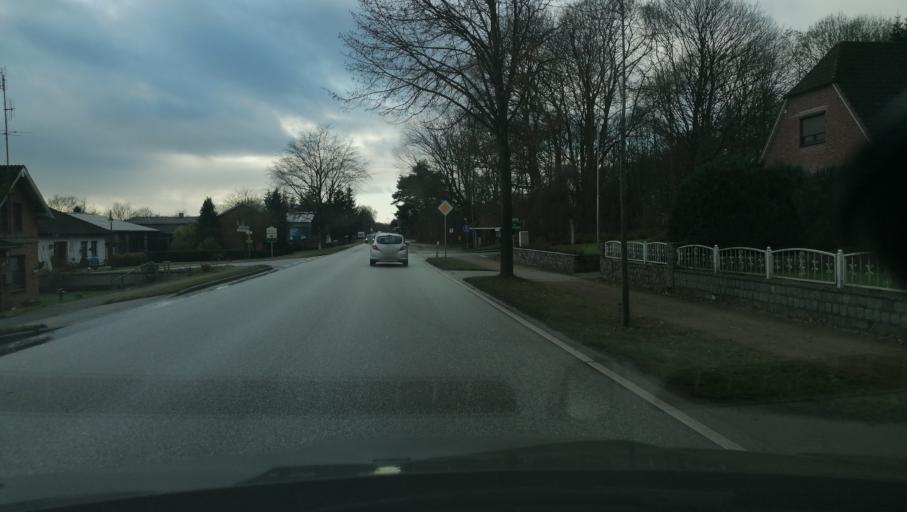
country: DE
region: Schleswig-Holstein
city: Bargenstedt
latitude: 54.0935
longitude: 9.1520
